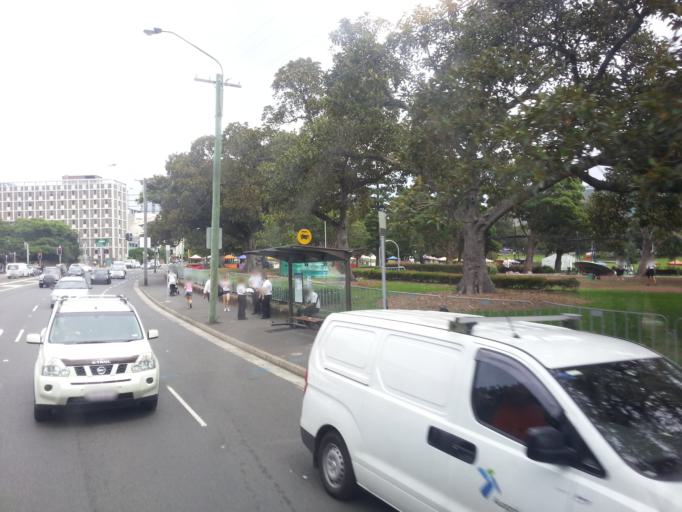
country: AU
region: New South Wales
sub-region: City of Sydney
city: Chippendale
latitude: -33.8869
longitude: 151.1937
